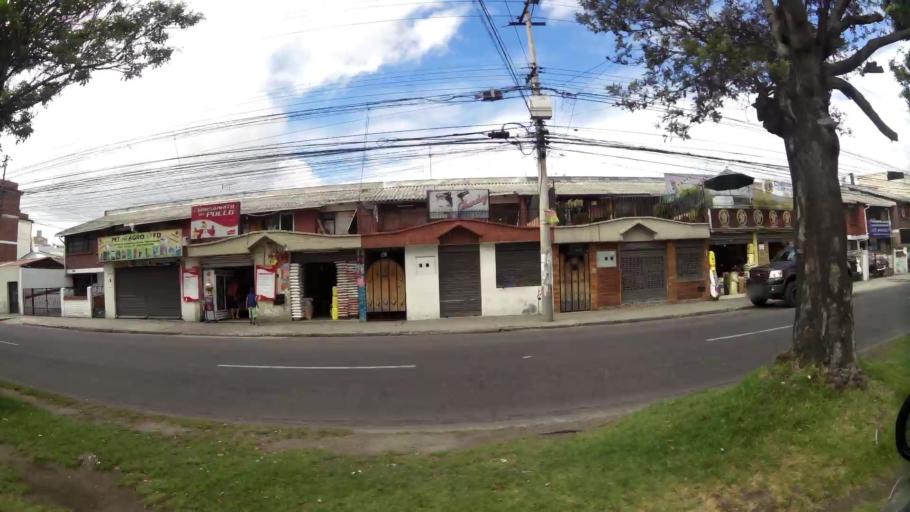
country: EC
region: Pichincha
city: Quito
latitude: -0.1543
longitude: -78.4721
